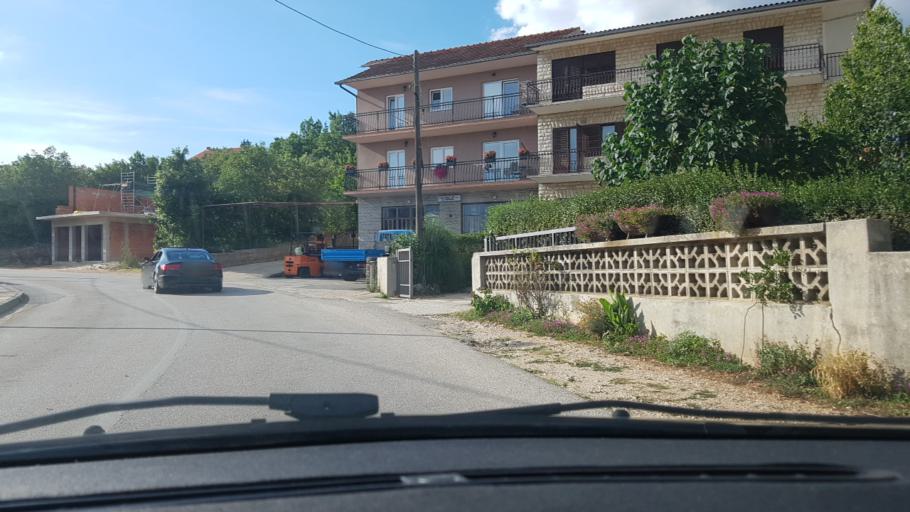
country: HR
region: Splitsko-Dalmatinska
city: Imotski
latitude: 43.4442
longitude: 17.2059
